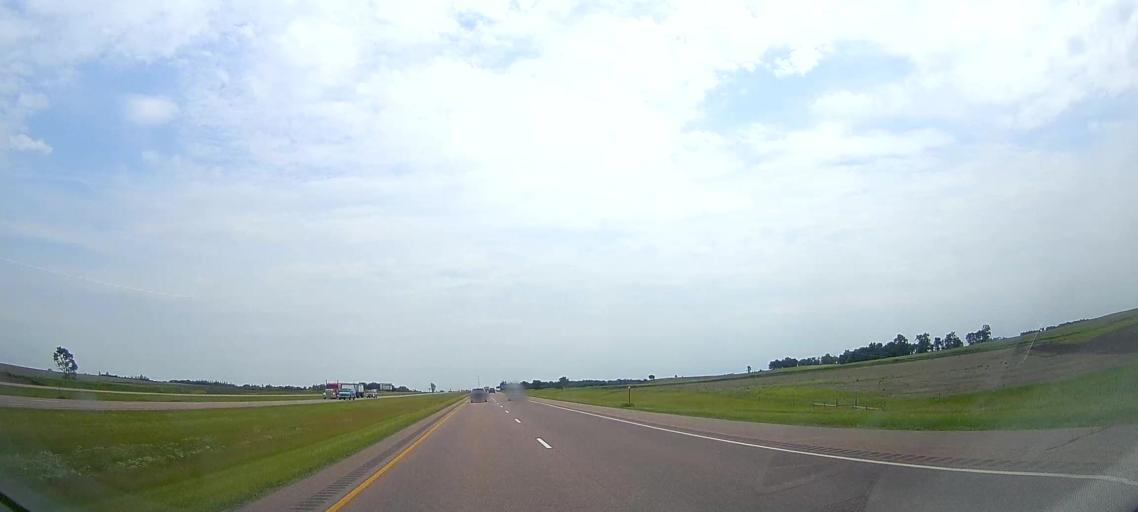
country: US
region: South Dakota
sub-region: Minnehaha County
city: Hartford
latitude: 43.6543
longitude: -97.1036
